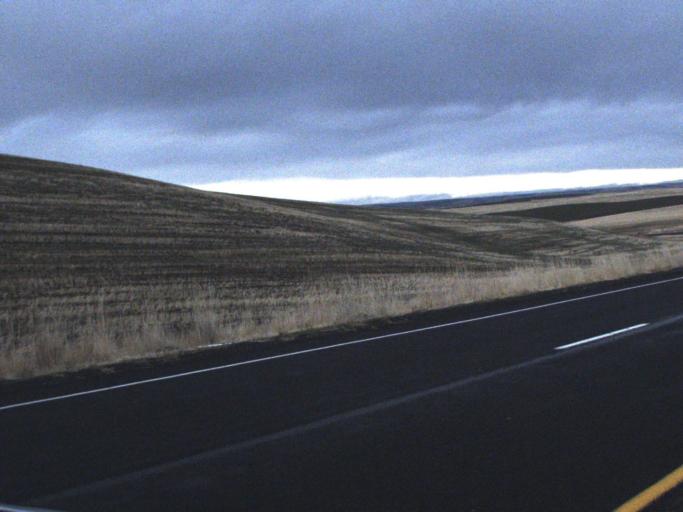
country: US
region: Washington
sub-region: Columbia County
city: Dayton
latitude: 46.3942
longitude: -117.9341
